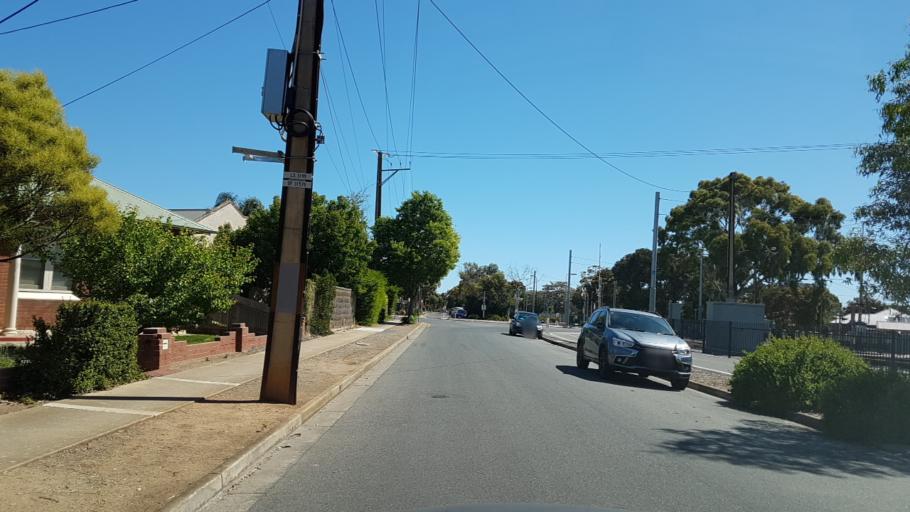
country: AU
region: South Australia
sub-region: Marion
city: South Plympton
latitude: -34.9628
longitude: 138.5642
